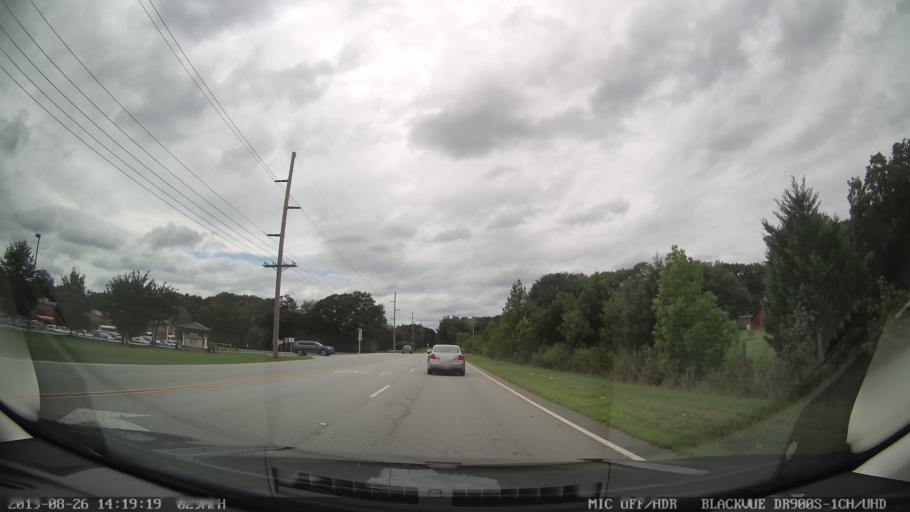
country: US
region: South Carolina
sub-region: Greenville County
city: Five Forks
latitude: 34.8013
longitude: -82.2414
